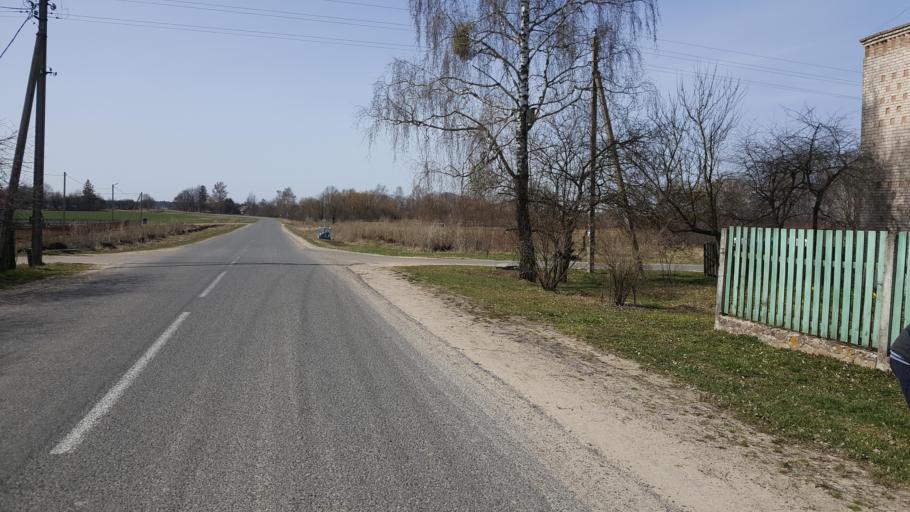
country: BY
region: Brest
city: Kamyanyets
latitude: 52.4664
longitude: 23.7303
